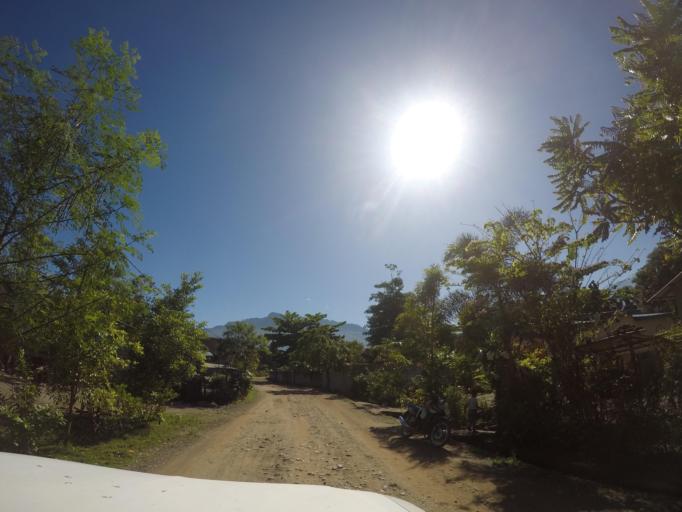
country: TL
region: Bobonaro
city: Maliana
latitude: -8.9918
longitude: 125.2122
